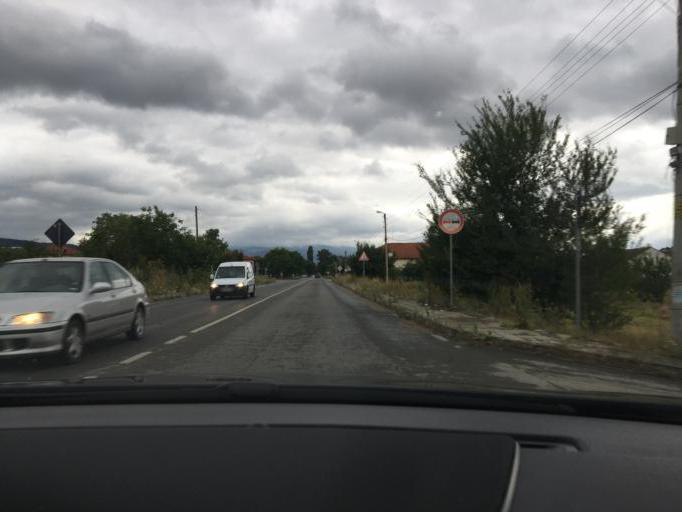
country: BG
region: Kyustendil
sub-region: Obshtina Kyustendil
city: Kyustendil
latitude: 42.2791
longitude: 22.7351
